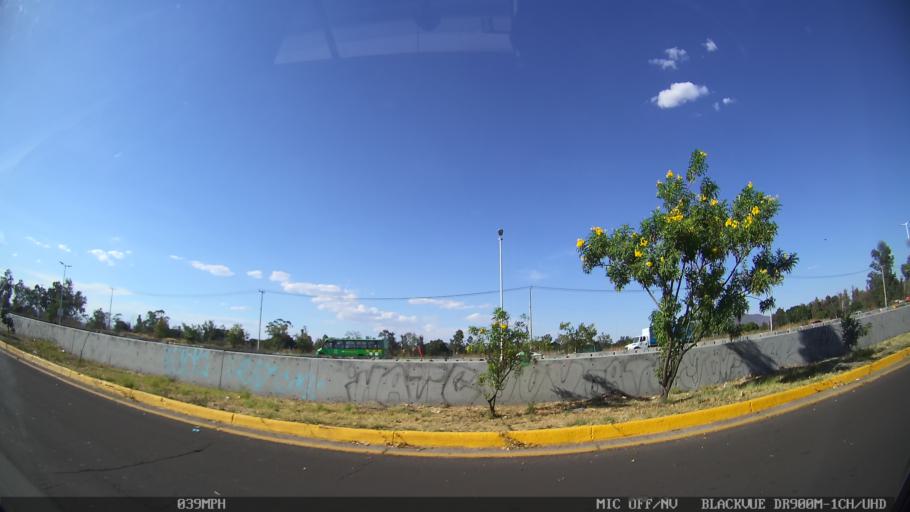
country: MX
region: Jalisco
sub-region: Zapopan
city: Zapopan
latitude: 20.7196
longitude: -103.3150
